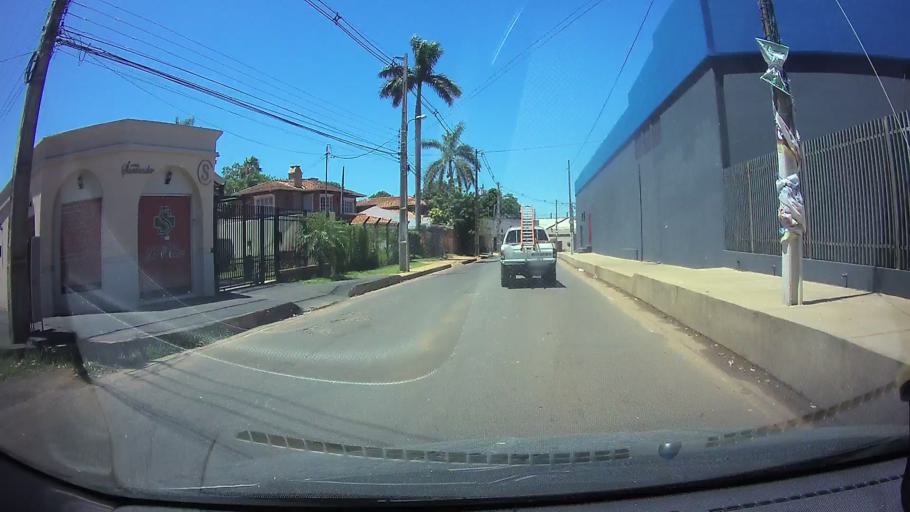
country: PY
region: Central
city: San Lorenzo
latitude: -25.3400
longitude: -57.4881
